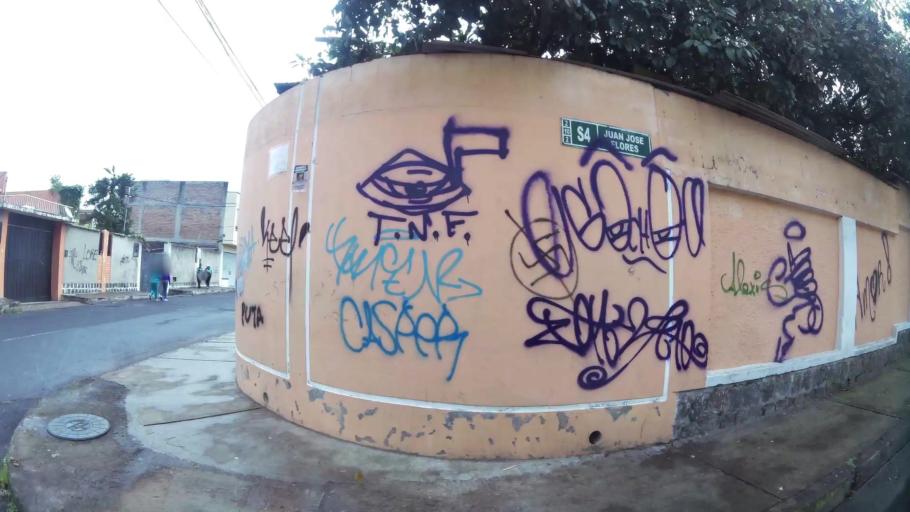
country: EC
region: Pichincha
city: Sangolqui
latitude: -0.2953
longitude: -78.4788
